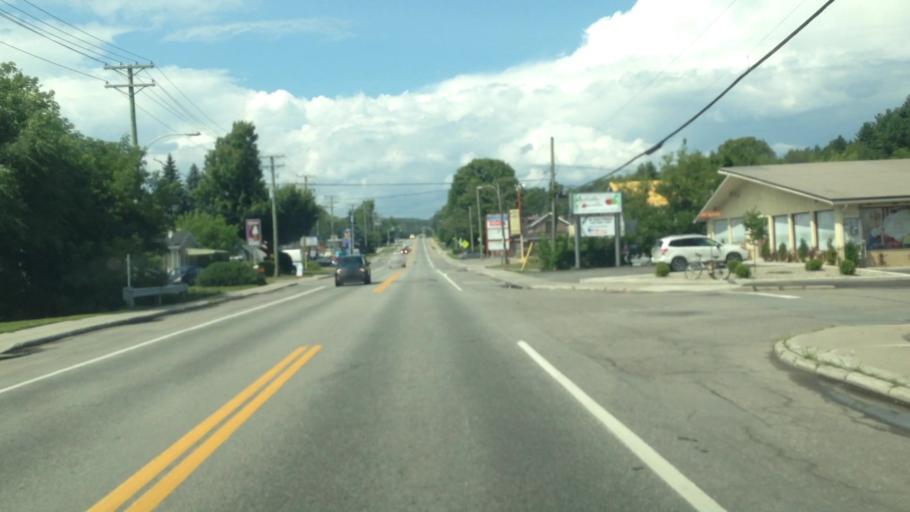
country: CA
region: Quebec
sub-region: Laurentides
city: Saint-Jerome
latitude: 45.8083
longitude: -74.0131
